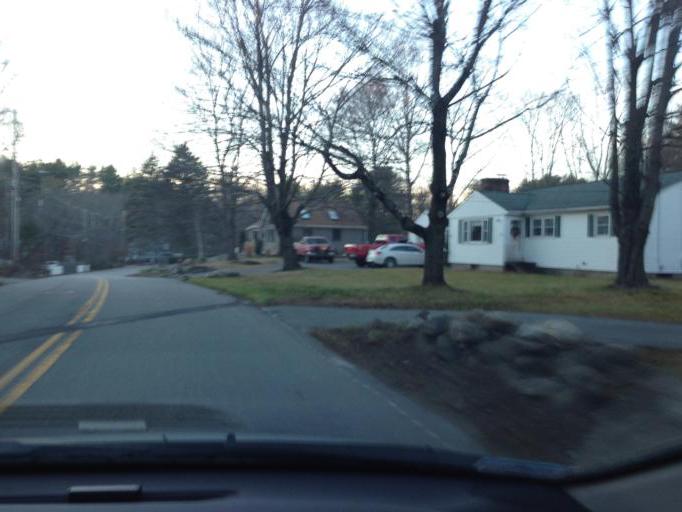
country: US
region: Massachusetts
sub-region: Middlesex County
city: Bedford
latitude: 42.4955
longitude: -71.2683
